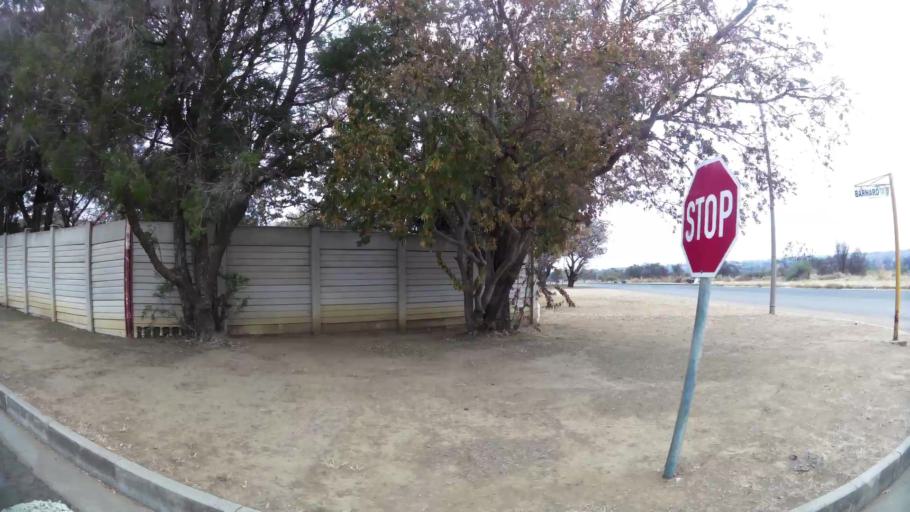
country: ZA
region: Orange Free State
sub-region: Fezile Dabi District Municipality
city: Kroonstad
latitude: -27.6691
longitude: 27.2532
